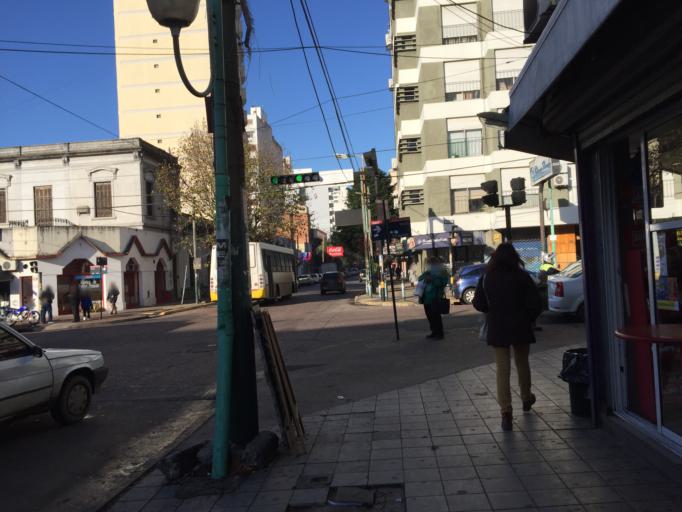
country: AR
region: Buenos Aires
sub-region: Partido de Lomas de Zamora
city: Lomas de Zamora
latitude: -34.7588
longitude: -58.4038
